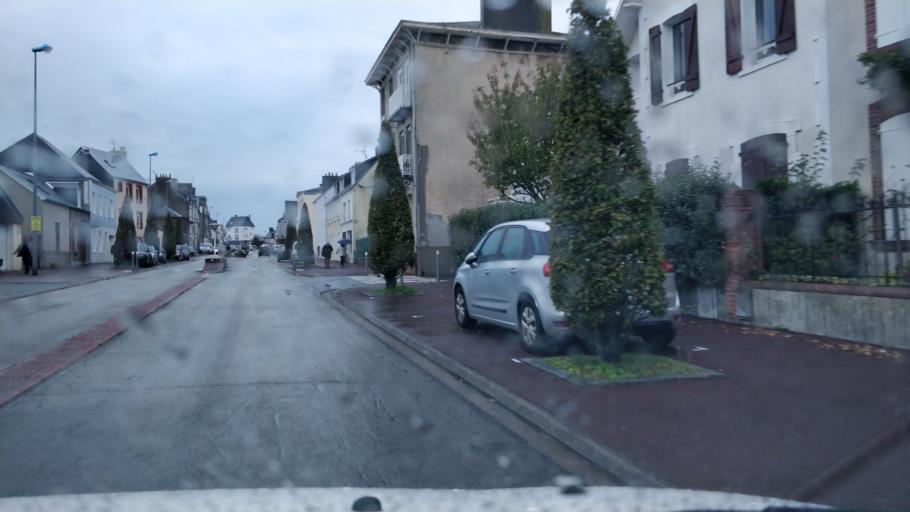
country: FR
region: Lower Normandy
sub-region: Departement de la Manche
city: Donville-les-Bains
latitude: 48.8365
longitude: -1.5817
